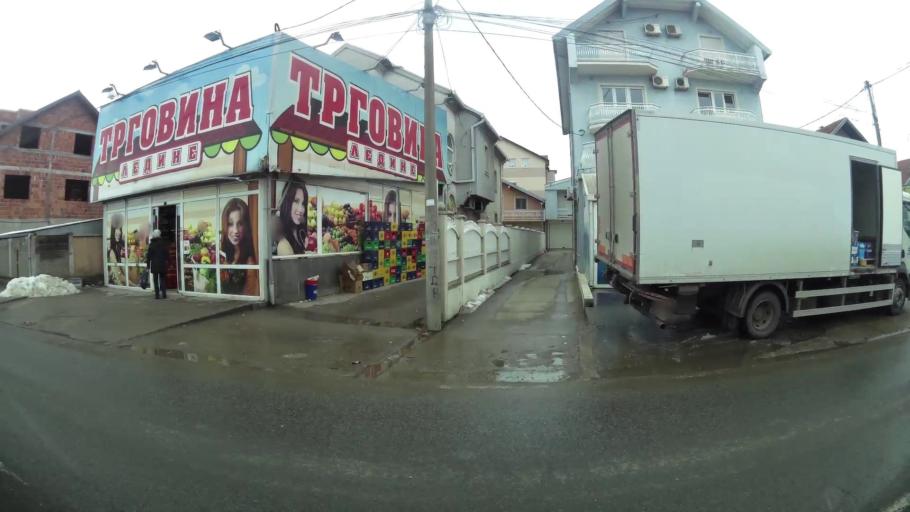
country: RS
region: Central Serbia
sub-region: Belgrade
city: Surcin
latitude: 44.8011
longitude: 20.3350
